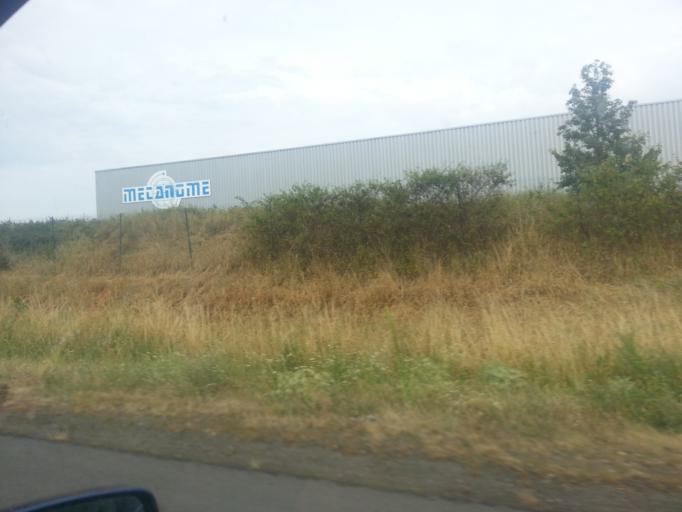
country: FR
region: Auvergne
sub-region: Departement du Puy-de-Dome
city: Cebazat
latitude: 45.8365
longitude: 3.1145
